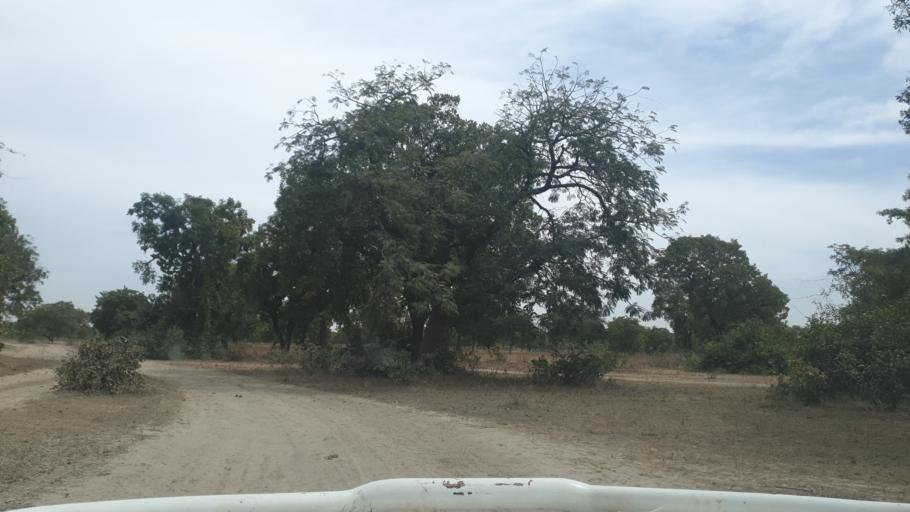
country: ML
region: Sikasso
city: Yorosso
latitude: 12.2379
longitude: -4.7379
